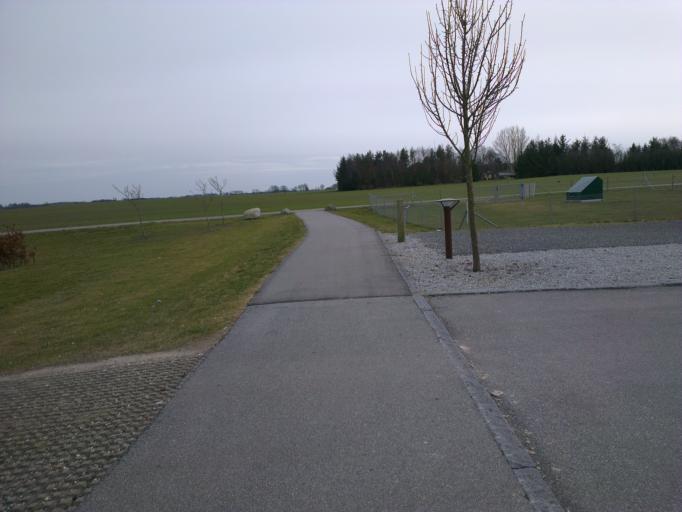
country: DK
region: Capital Region
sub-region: Frederikssund Kommune
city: Frederikssund
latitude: 55.8175
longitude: 12.0793
